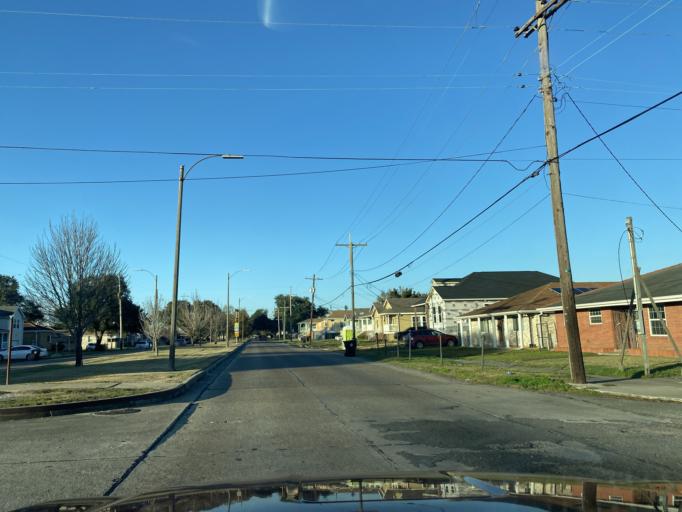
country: US
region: Louisiana
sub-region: Orleans Parish
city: New Orleans
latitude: 30.0173
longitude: -90.0514
